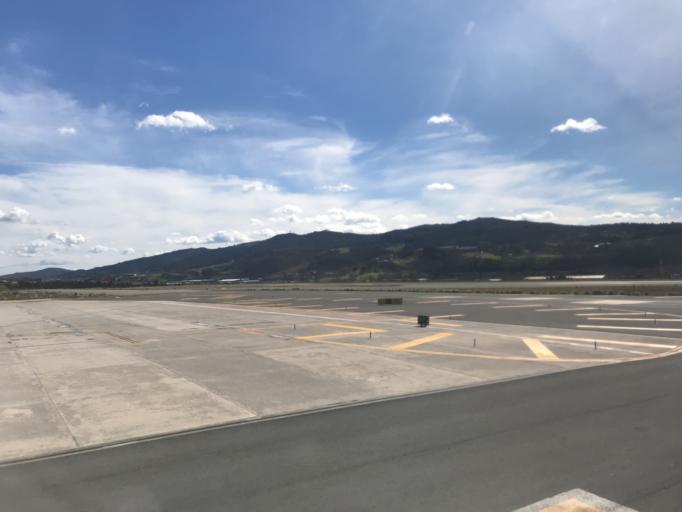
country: ES
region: Basque Country
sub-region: Bizkaia
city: Sondika
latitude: 43.3019
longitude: -2.9056
